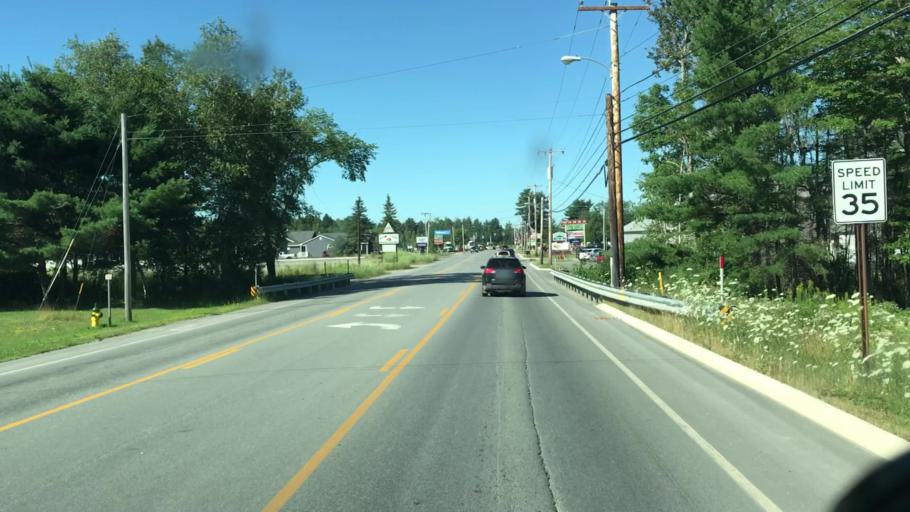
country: US
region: Maine
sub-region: Penobscot County
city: Lincoln
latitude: 45.3589
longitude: -68.5233
